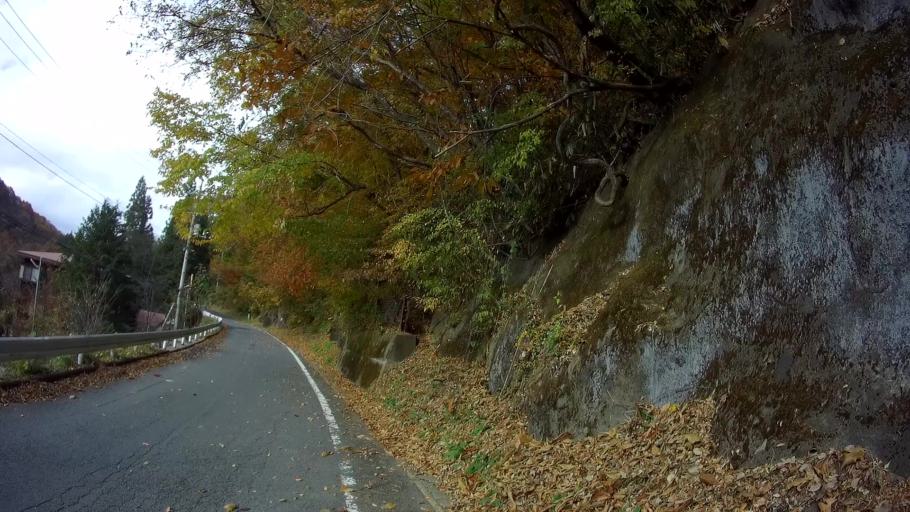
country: JP
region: Gunma
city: Nakanojomachi
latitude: 36.6399
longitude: 138.6511
